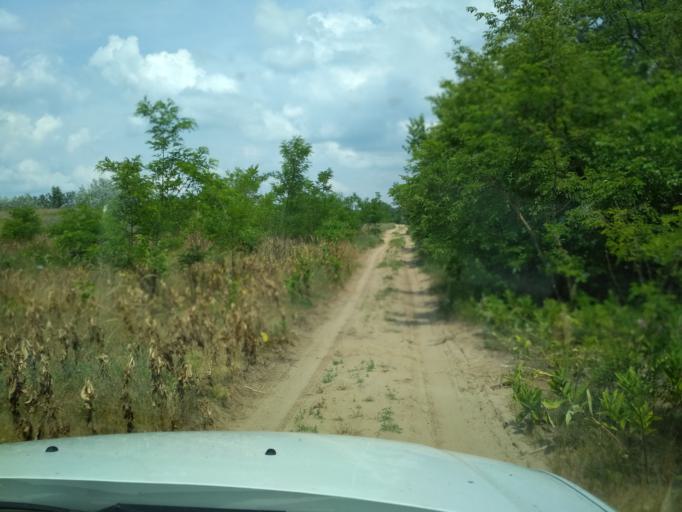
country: HU
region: Pest
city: Tapioszentmarton
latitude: 47.3662
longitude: 19.7756
